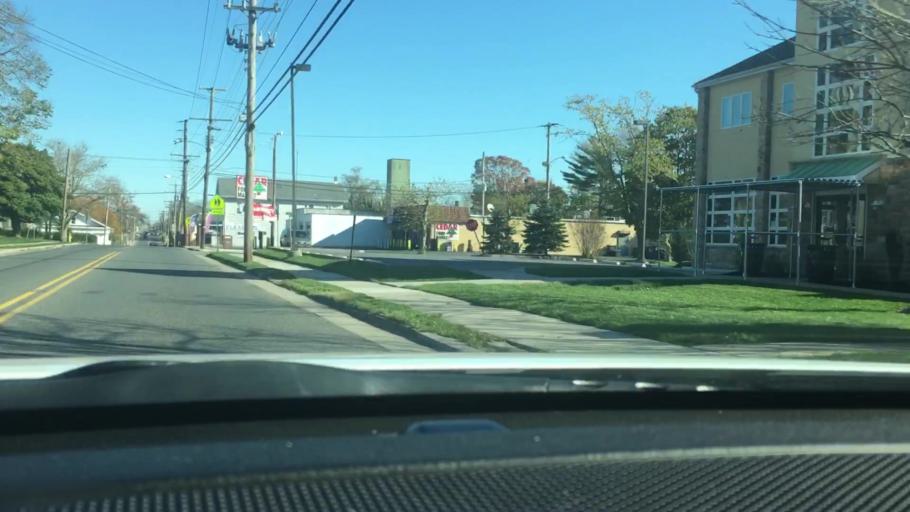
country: US
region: New Jersey
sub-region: Atlantic County
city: Pleasantville
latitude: 39.3829
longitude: -74.5305
